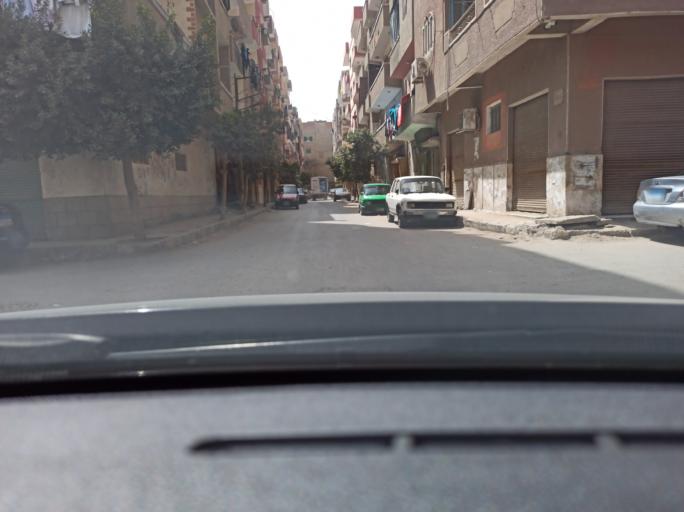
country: EG
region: Muhafazat Bani Suwayf
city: Bani Suwayf
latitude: 29.0825
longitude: 31.0885
